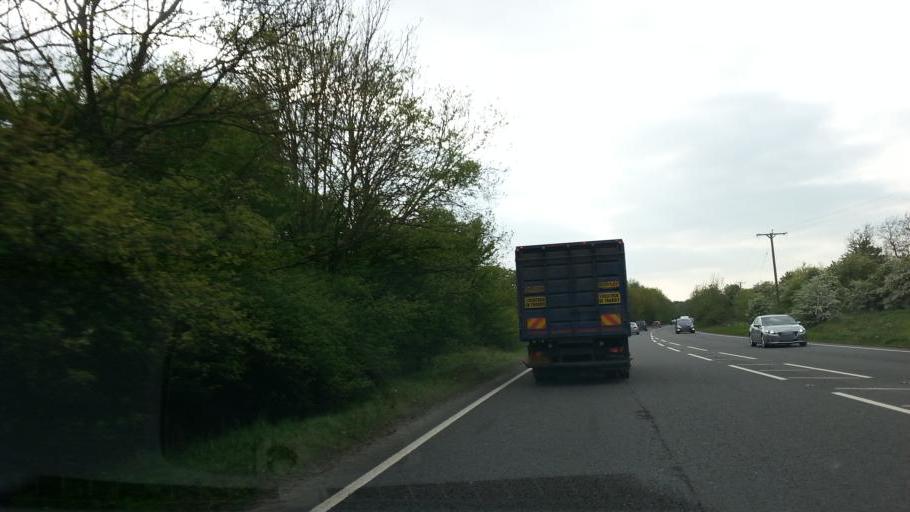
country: GB
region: England
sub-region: Nottinghamshire
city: South Collingham
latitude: 53.0769
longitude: -0.7024
